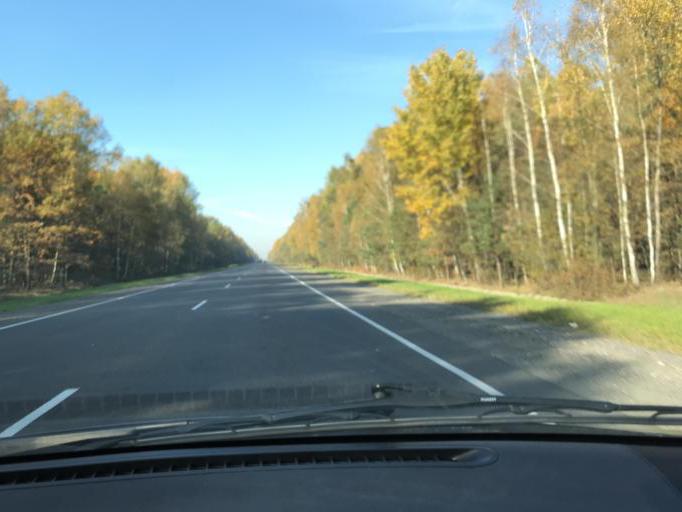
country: BY
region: Brest
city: Horad Luninyets
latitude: 52.3052
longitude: 26.6981
